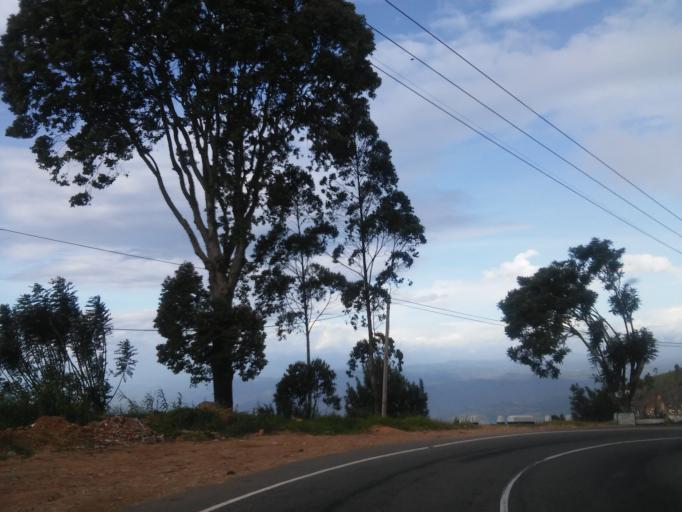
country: LK
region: Uva
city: Haputale
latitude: 6.7616
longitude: 80.9524
